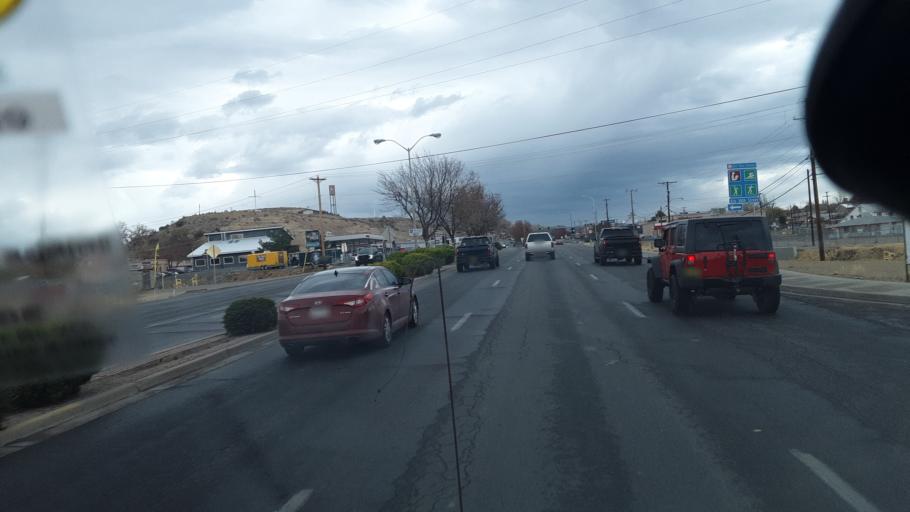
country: US
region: New Mexico
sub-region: San Juan County
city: Farmington
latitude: 36.7567
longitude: -108.1562
